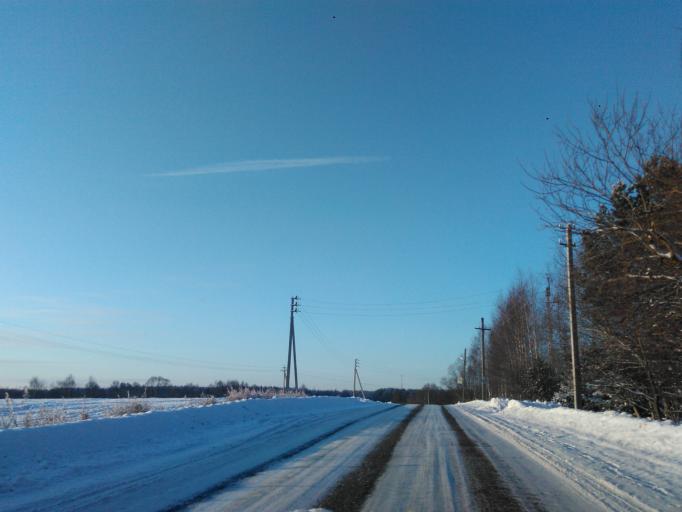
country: RU
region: Tverskaya
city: Zavidovo
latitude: 56.6080
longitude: 36.5751
